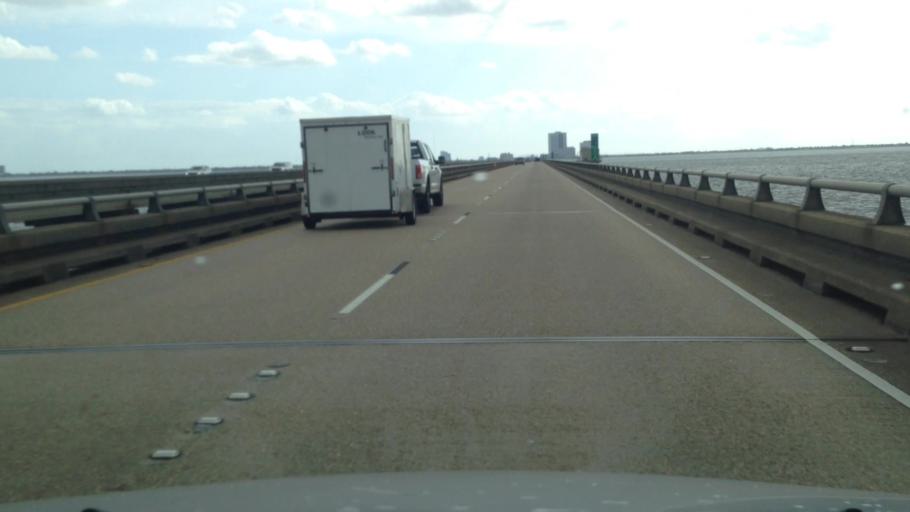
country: US
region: Louisiana
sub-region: Jefferson Parish
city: Metairie
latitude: 30.0566
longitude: -90.1480
